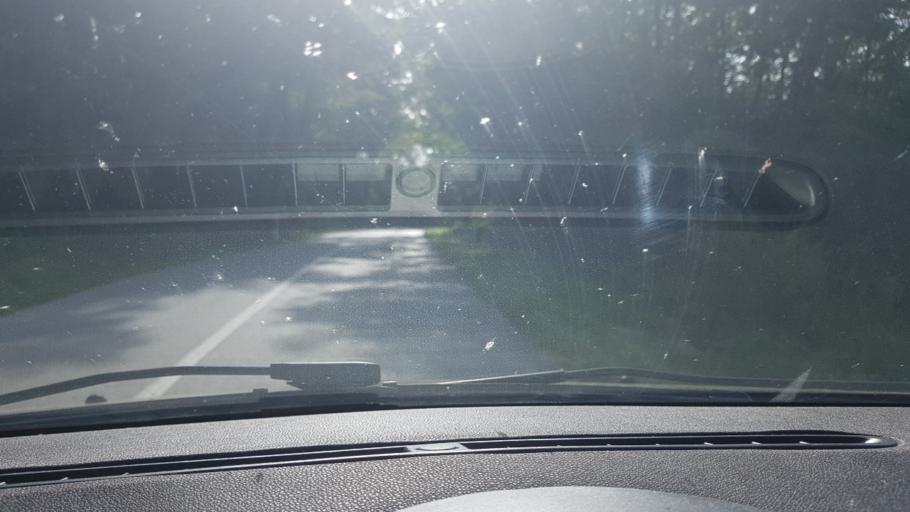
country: HR
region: Krapinsko-Zagorska
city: Zlatar
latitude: 46.1209
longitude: 16.1024
